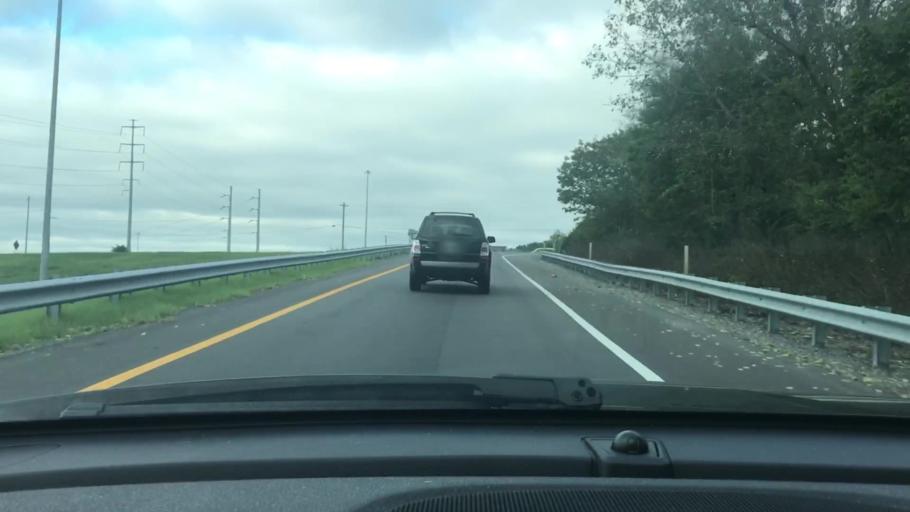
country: US
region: Tennessee
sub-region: Davidson County
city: Goodlettsville
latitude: 36.3096
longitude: -86.6944
